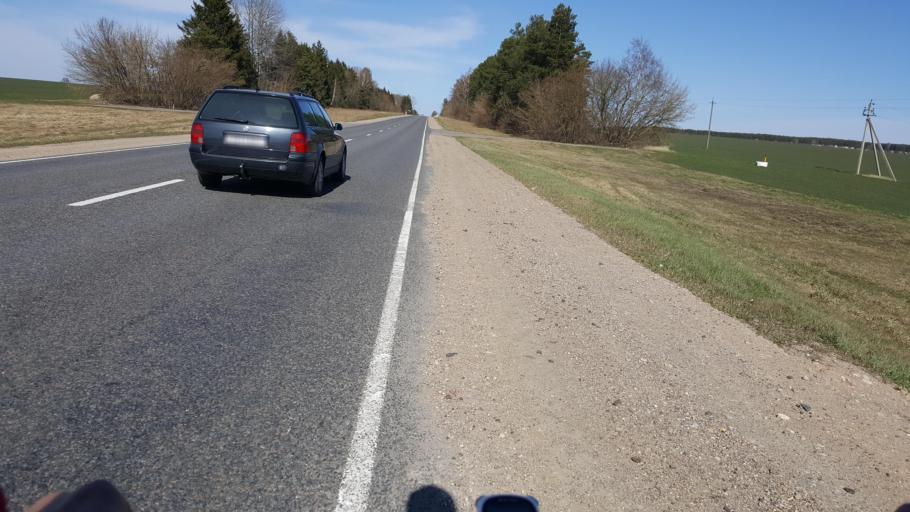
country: BY
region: Brest
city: Kamyanyets
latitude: 52.3627
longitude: 23.7823
